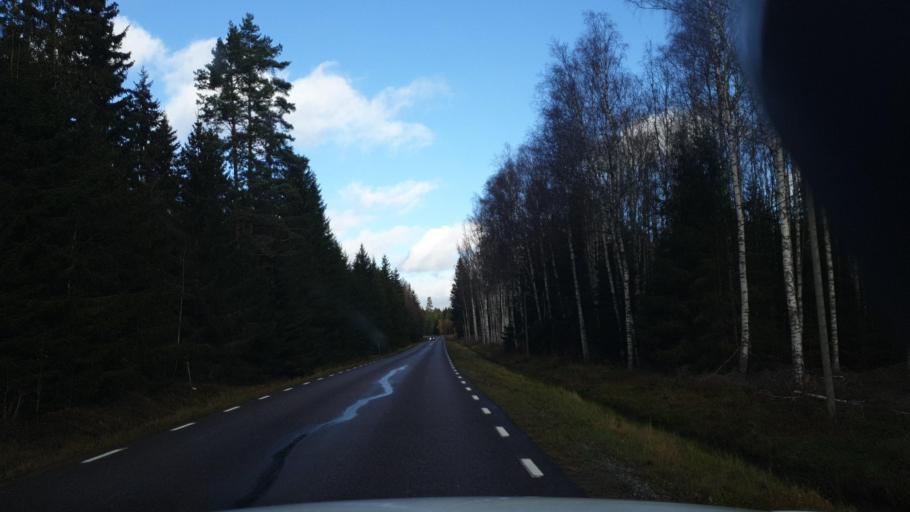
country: SE
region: Vaermland
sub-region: Grums Kommun
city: Slottsbron
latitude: 59.4863
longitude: 12.8824
